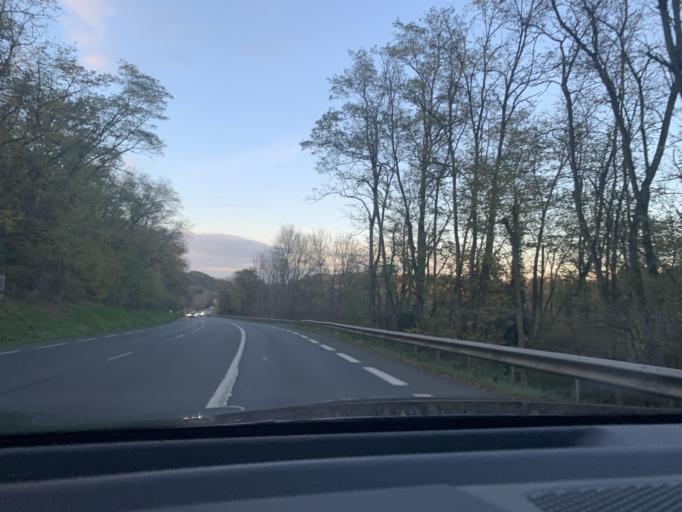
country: FR
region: Rhone-Alpes
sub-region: Departement du Rhone
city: Liergues
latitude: 45.9458
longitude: 4.6610
